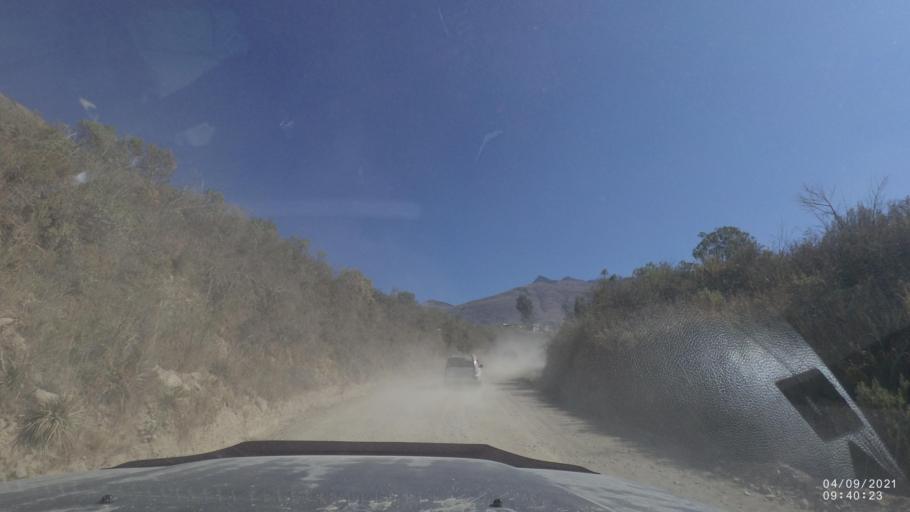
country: BO
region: Cochabamba
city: Sipe Sipe
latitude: -17.3426
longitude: -66.3870
